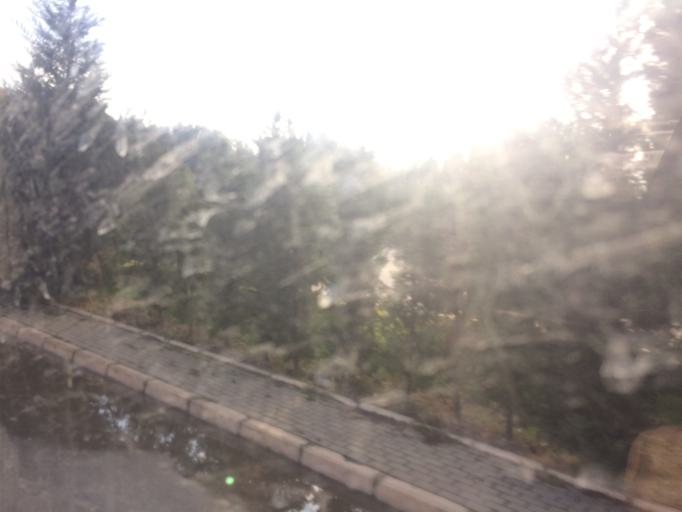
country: TR
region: Izmir
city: Karsiyaka
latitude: 38.4884
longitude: 26.9584
